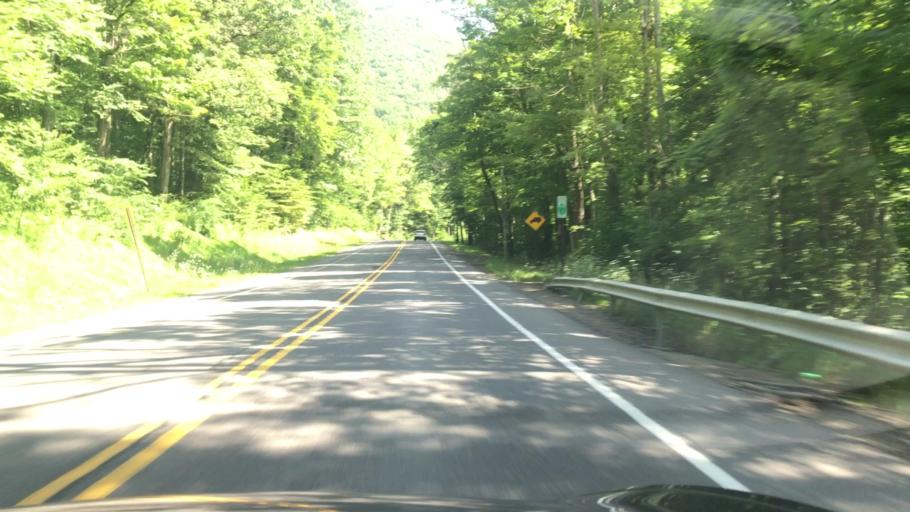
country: US
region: Pennsylvania
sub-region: Lycoming County
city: Garden View
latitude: 41.4122
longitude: -77.0439
